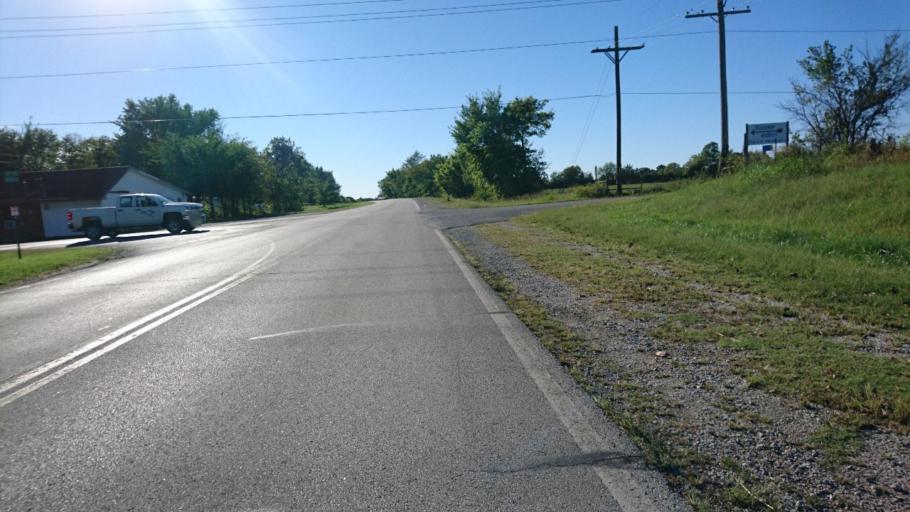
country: US
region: Missouri
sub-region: Jasper County
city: Carthage
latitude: 37.1734
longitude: -94.3649
